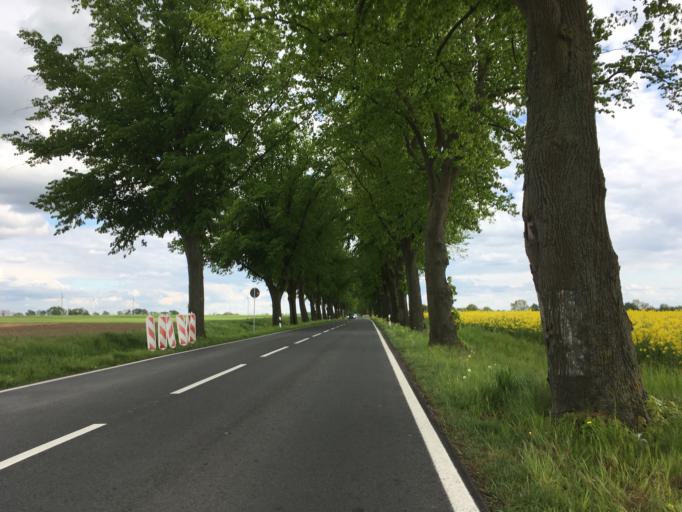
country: DE
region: Brandenburg
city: Ahrensfelde
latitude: 52.6177
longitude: 13.6129
